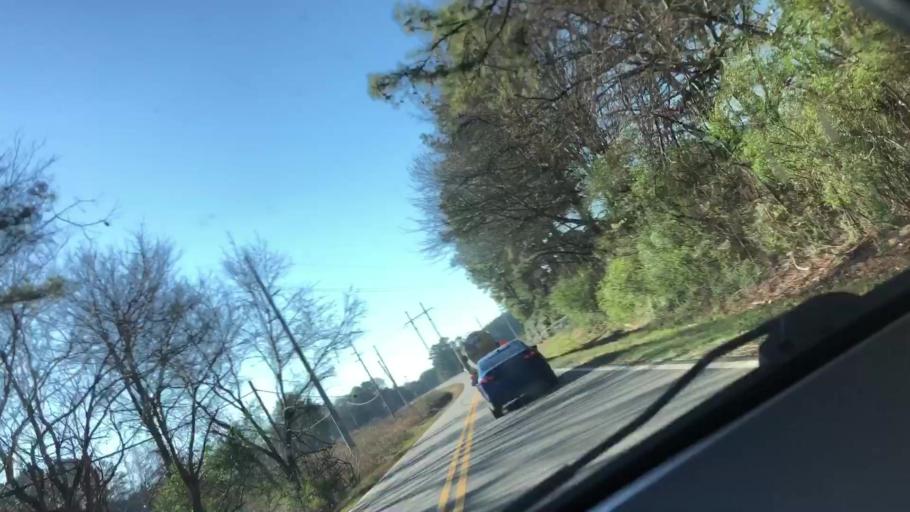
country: US
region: Georgia
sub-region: Bartow County
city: Cartersville
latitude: 34.2153
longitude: -84.8021
